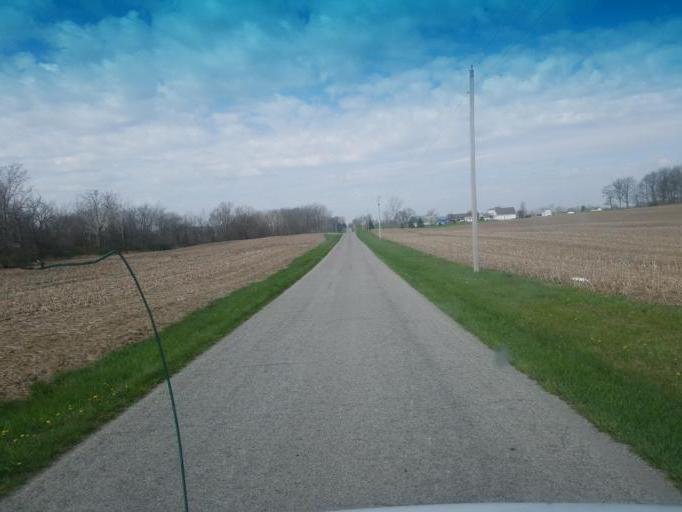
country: US
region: Ohio
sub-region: Logan County
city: Northwood
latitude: 40.4918
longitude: -83.7247
